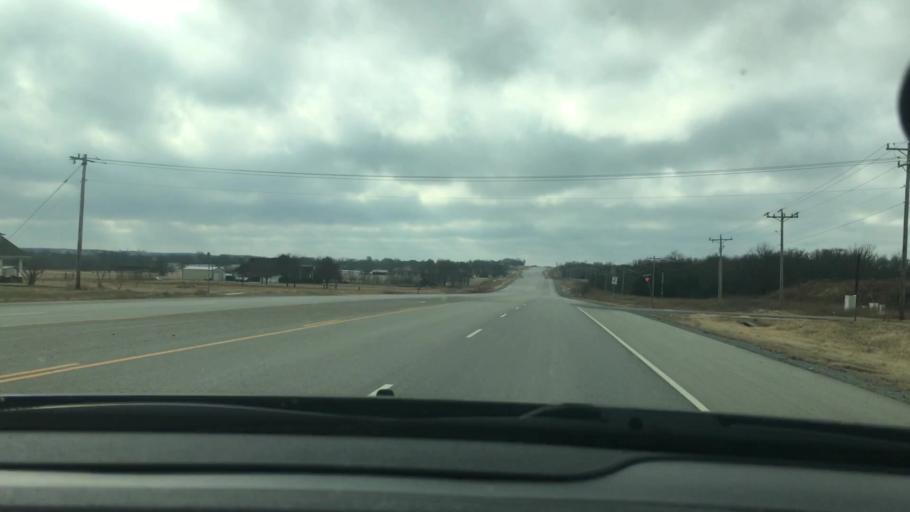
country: US
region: Oklahoma
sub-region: Bryan County
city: Durant
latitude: 34.0708
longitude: -96.3731
